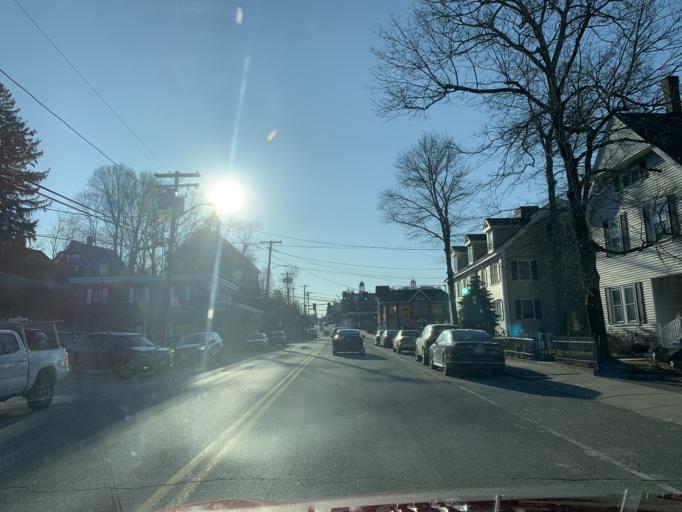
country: US
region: Massachusetts
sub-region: Essex County
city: Andover
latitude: 42.6590
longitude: -71.1427
